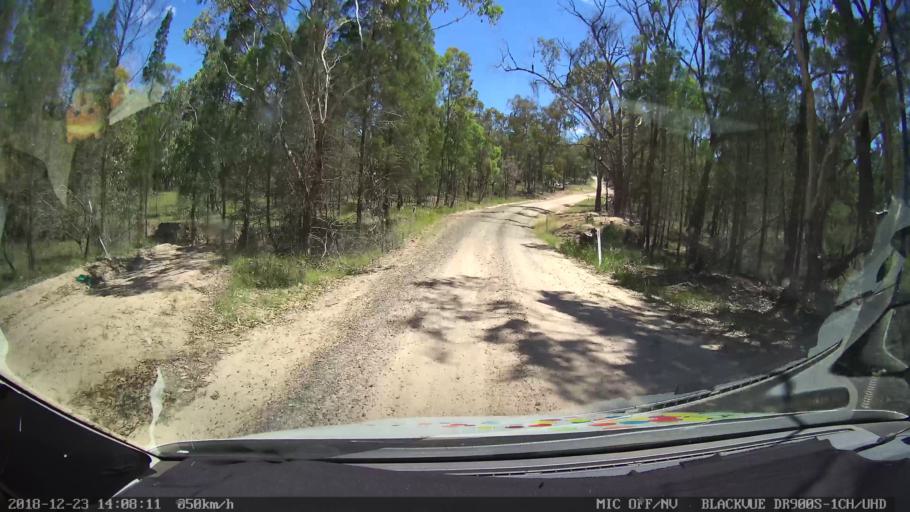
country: AU
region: New South Wales
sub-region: Tamworth Municipality
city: Manilla
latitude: -30.6407
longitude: 151.0694
